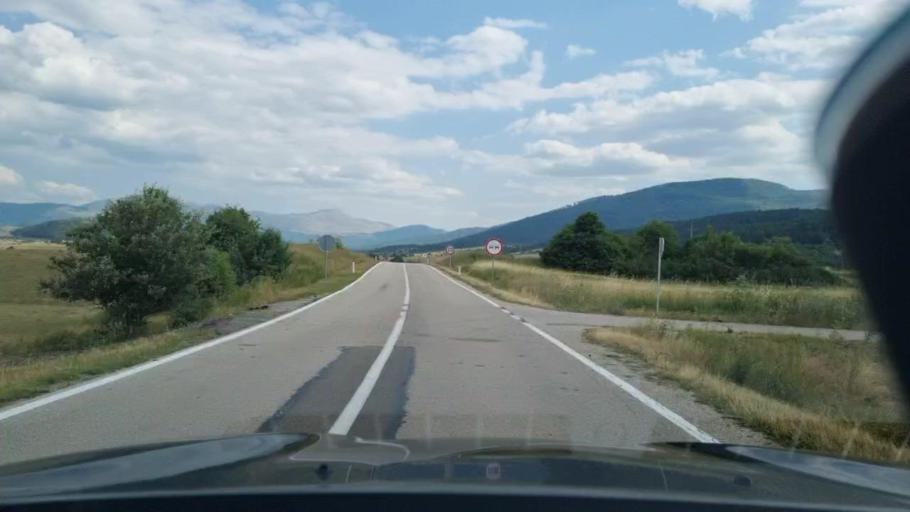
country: BA
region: Federation of Bosnia and Herzegovina
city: Bosansko Grahovo
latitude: 44.1685
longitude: 16.3758
